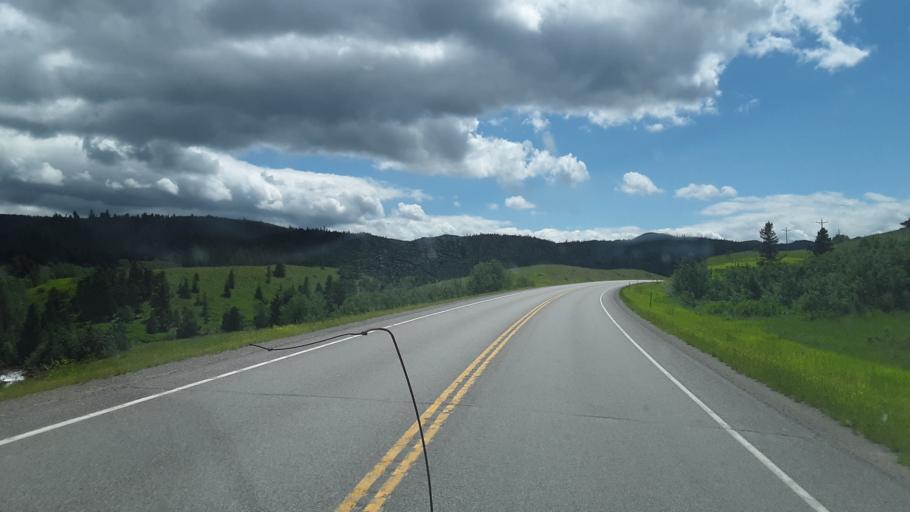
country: US
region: Montana
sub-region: Glacier County
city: South Browning
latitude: 48.4235
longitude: -113.2121
